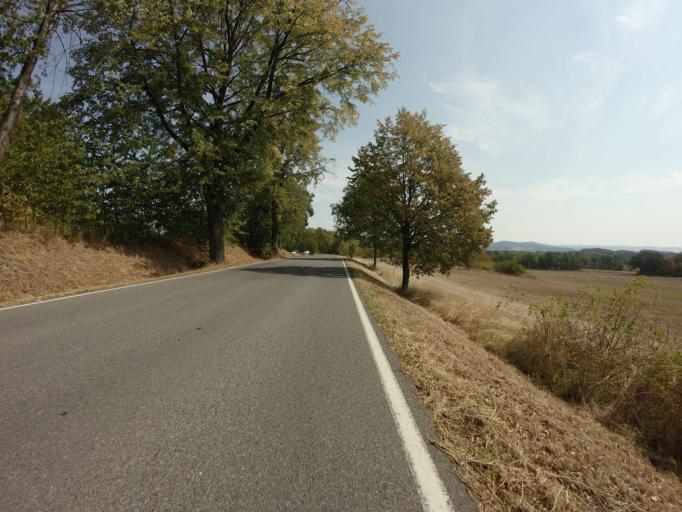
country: CZ
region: Central Bohemia
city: Sedlcany
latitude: 49.6172
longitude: 14.4000
